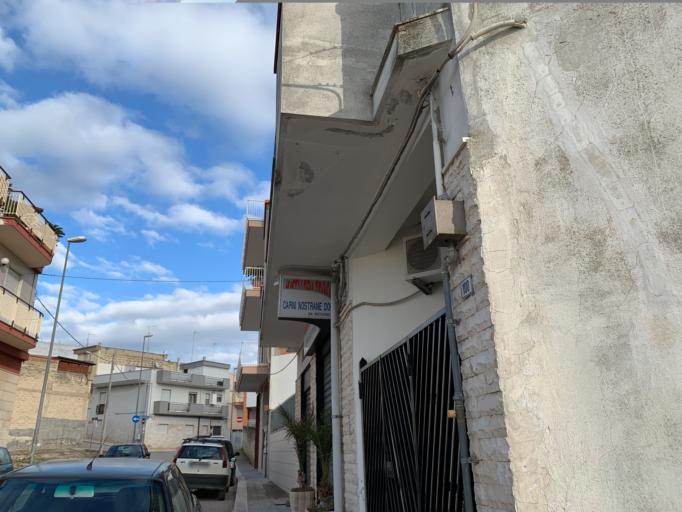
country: IT
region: Apulia
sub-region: Provincia di Barletta - Andria - Trani
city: Andria
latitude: 41.2308
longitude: 16.2839
